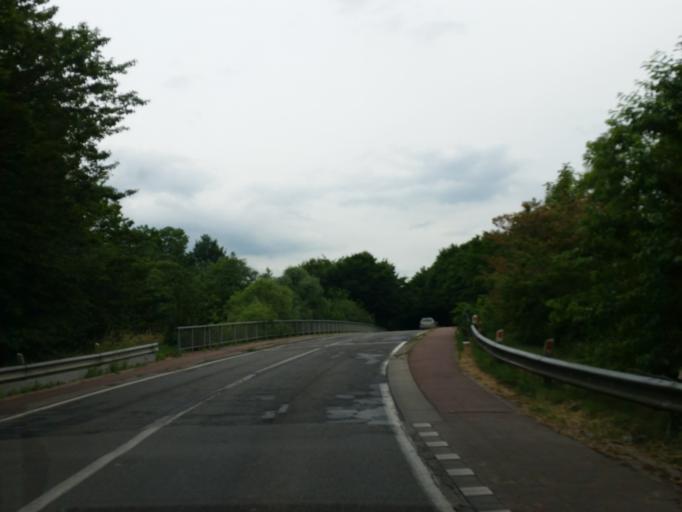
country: BE
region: Flanders
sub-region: Provincie Antwerpen
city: Ranst
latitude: 51.1976
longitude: 4.6018
